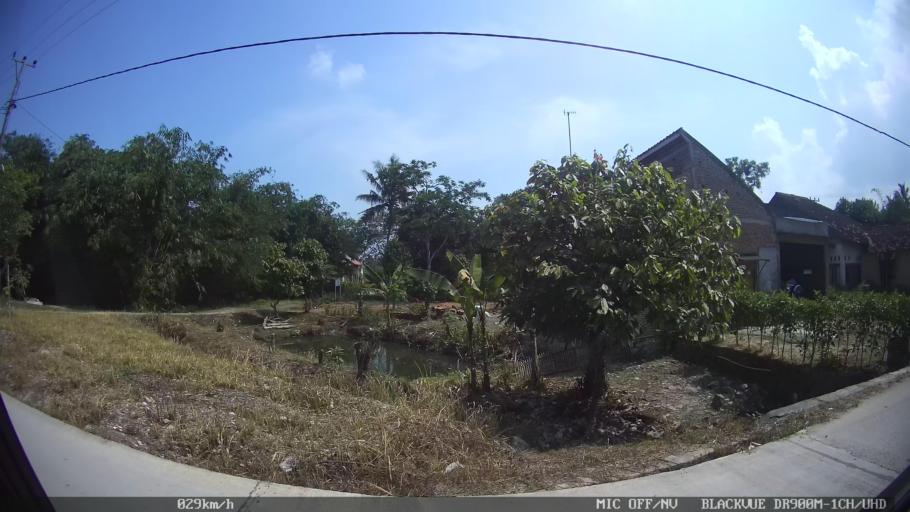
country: ID
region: Lampung
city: Natar
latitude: -5.2658
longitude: 105.1895
